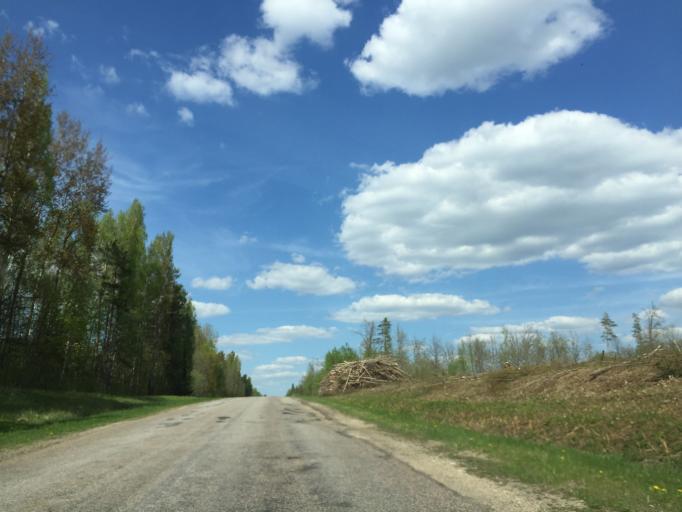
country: LV
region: Limbazu Rajons
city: Limbazi
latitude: 57.4099
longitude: 24.6938
